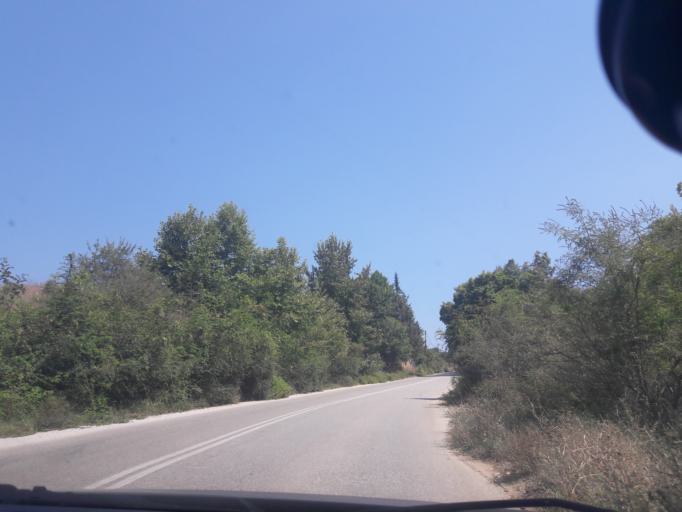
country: GR
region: Central Macedonia
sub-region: Nomos Chalkidikis
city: Megali Panagia
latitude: 40.3700
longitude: 23.6532
